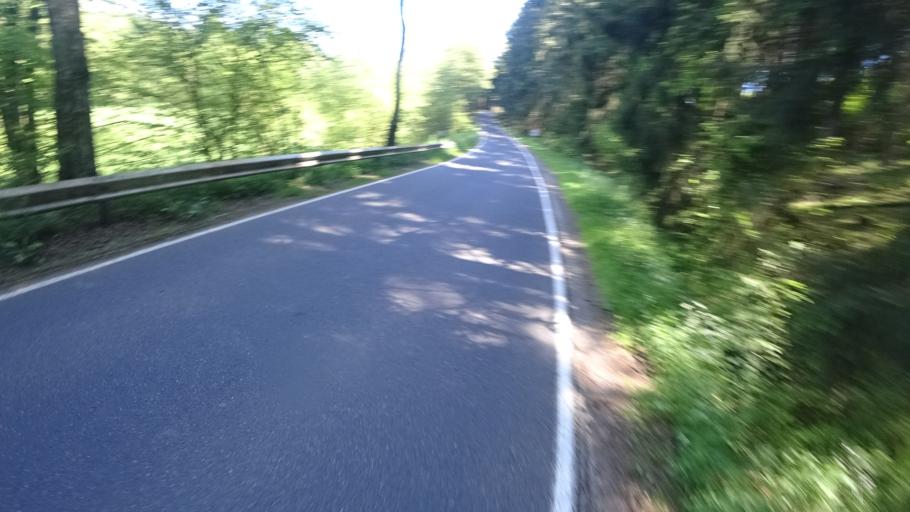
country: DE
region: Rheinland-Pfalz
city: Elben
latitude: 50.7468
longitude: 7.8383
